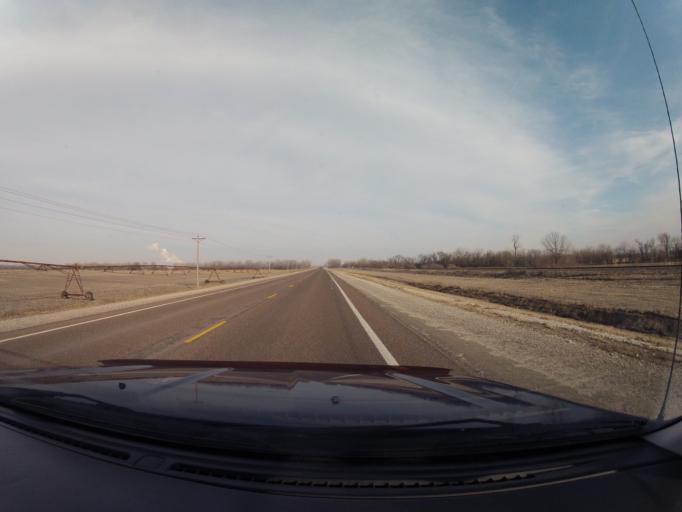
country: US
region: Kansas
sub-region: Pottawatomie County
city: Wamego
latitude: 39.2113
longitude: -96.2467
